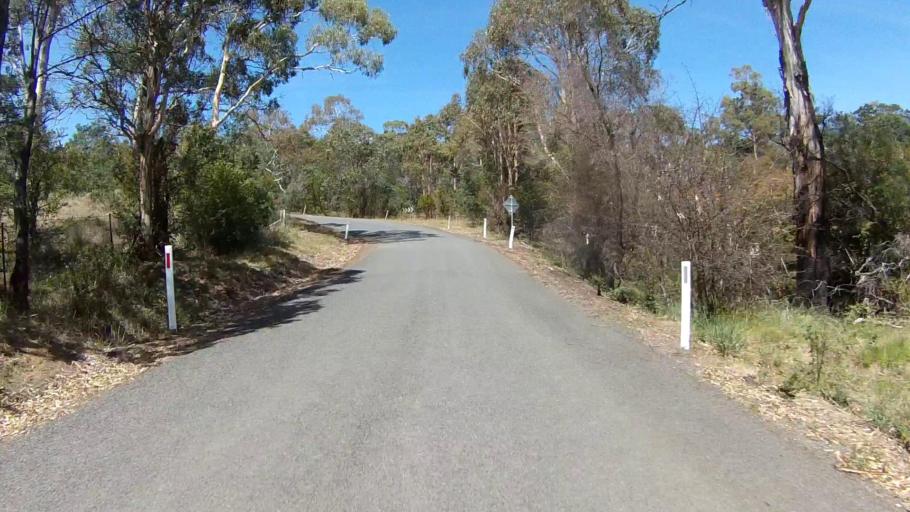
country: AU
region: Tasmania
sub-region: Sorell
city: Sorell
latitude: -42.7646
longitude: 147.6486
